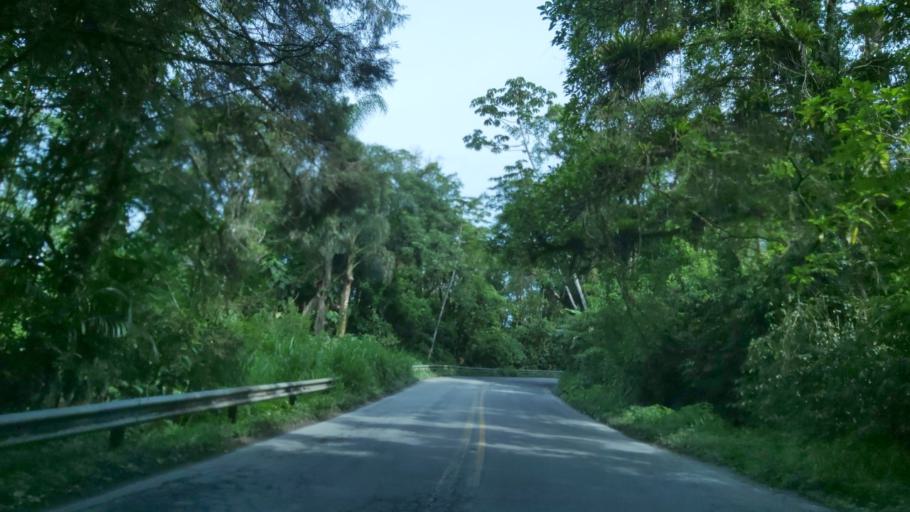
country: BR
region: Sao Paulo
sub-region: Miracatu
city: Miracatu
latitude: -24.0415
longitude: -47.5679
